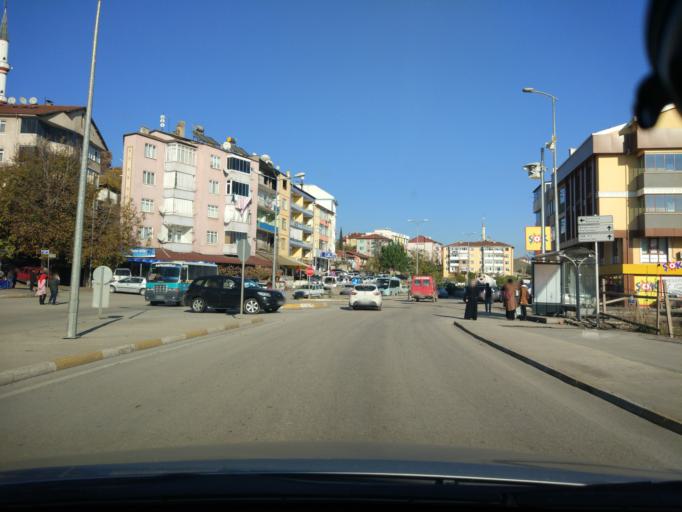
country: TR
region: Karabuk
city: Karabuk
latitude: 41.2108
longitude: 32.6415
